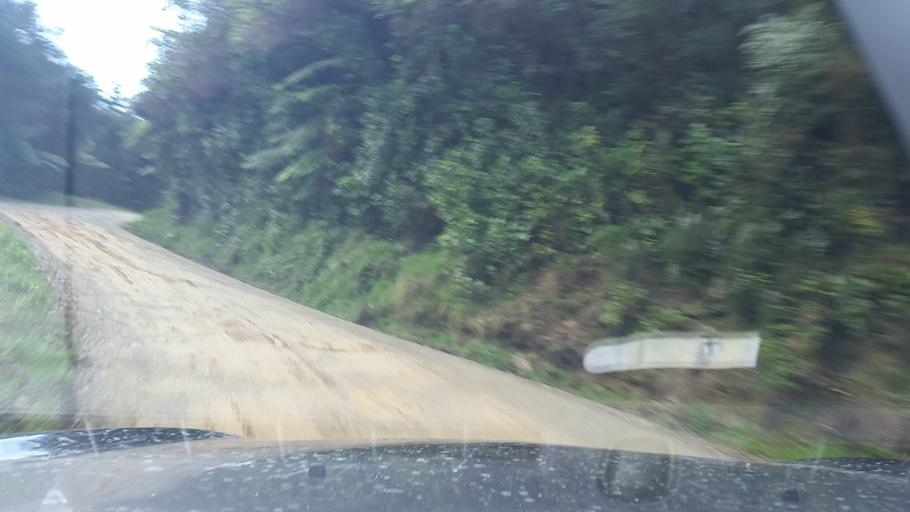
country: NZ
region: Marlborough
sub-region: Marlborough District
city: Picton
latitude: -41.1383
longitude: 174.1414
